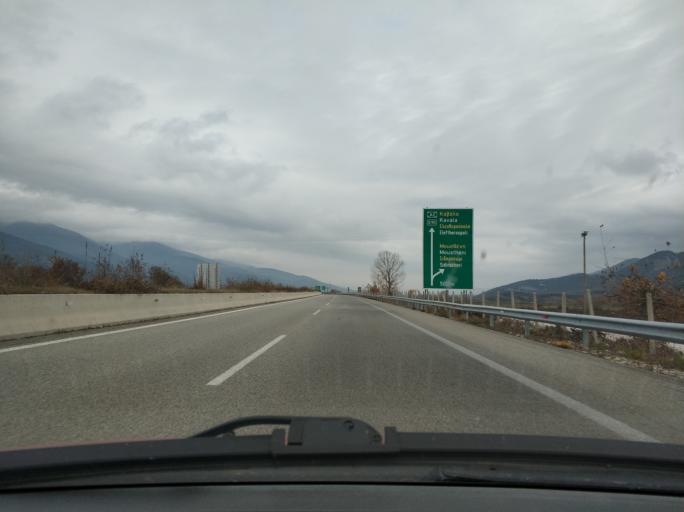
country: GR
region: East Macedonia and Thrace
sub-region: Nomos Kavalas
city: Nikisiani
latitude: 40.8340
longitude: 24.1081
